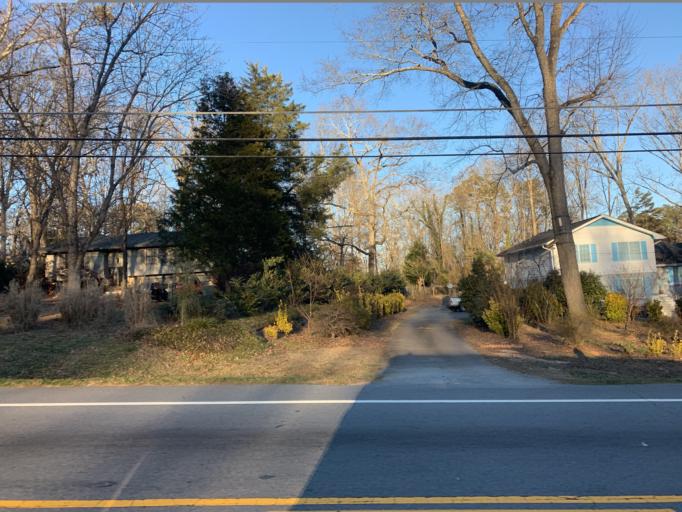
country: US
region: Georgia
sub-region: Gwinnett County
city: Mountain Park
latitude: 33.8755
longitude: -84.1068
